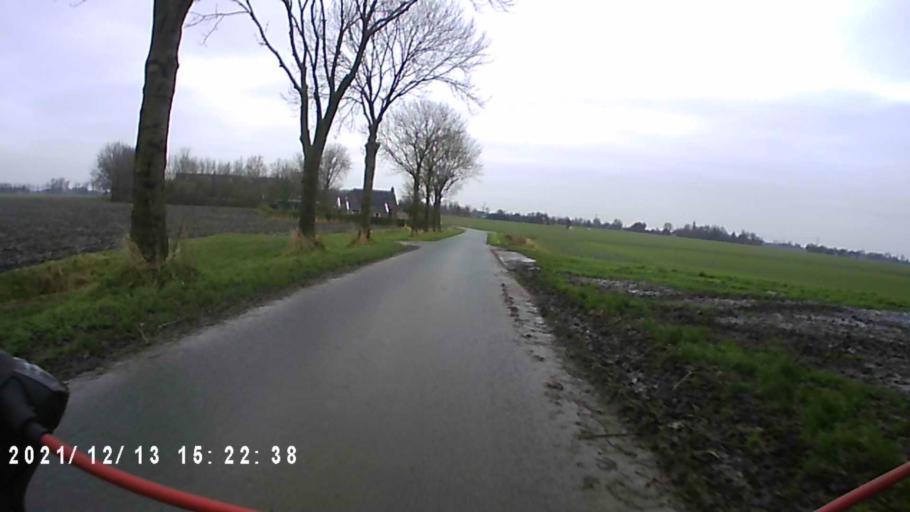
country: NL
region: Groningen
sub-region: Gemeente Appingedam
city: Appingedam
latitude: 53.3431
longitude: 6.7870
